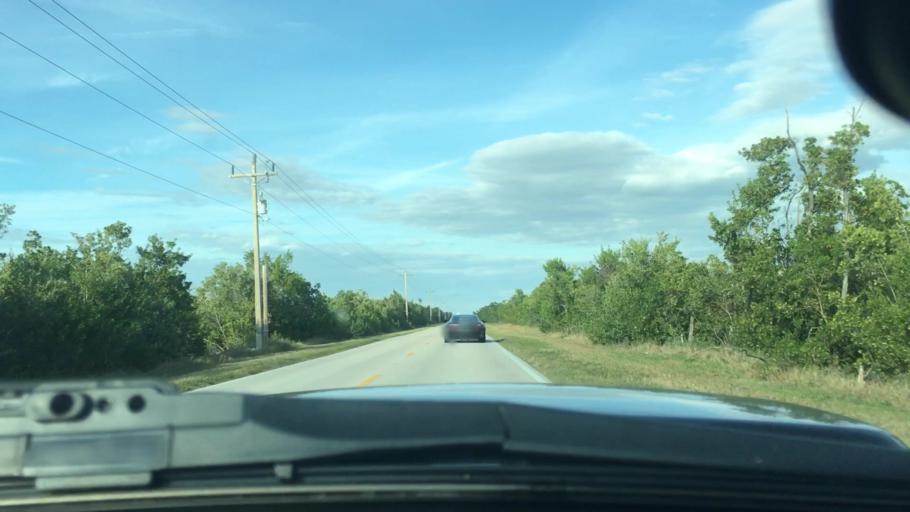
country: US
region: Florida
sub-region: Collier County
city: Marco
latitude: 25.9504
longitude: -81.6417
